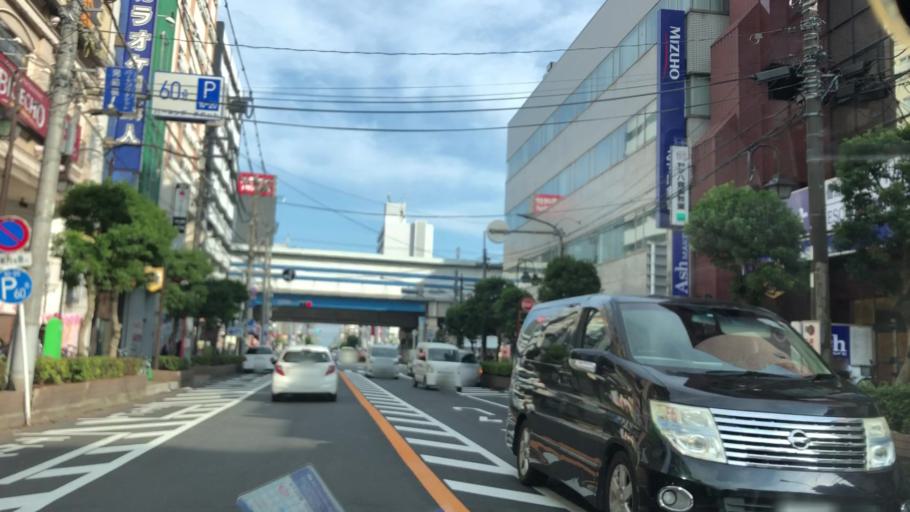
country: JP
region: Tokyo
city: Urayasu
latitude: 35.6840
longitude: 139.9139
